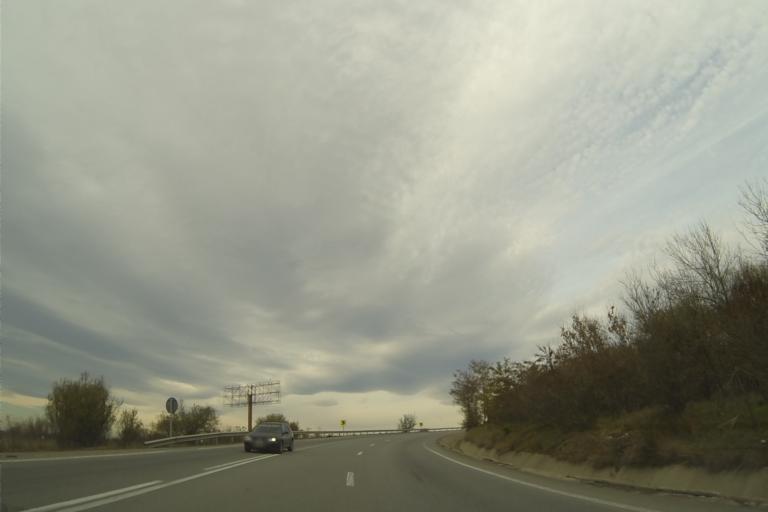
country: RO
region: Olt
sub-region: Comuna Valea Mare
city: Valea Mare
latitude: 44.4883
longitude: 24.4424
